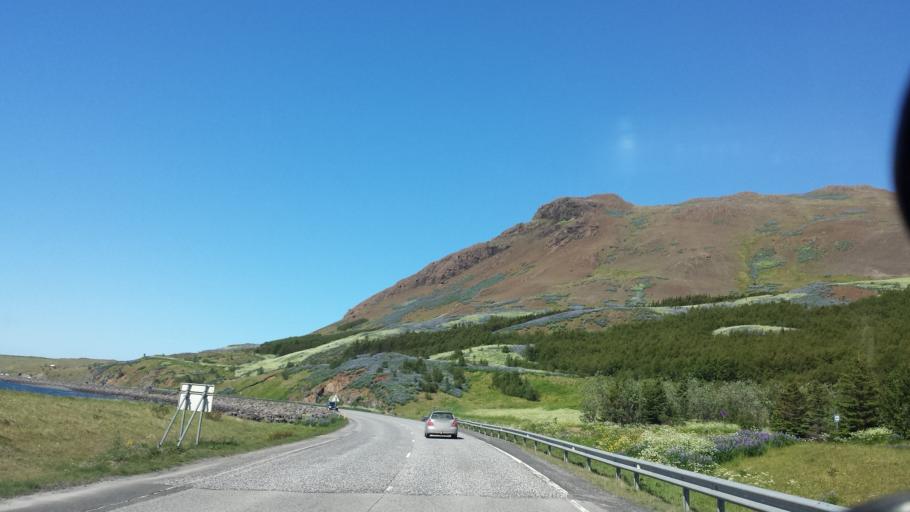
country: IS
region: Capital Region
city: Mosfellsbaer
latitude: 64.2082
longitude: -21.7147
